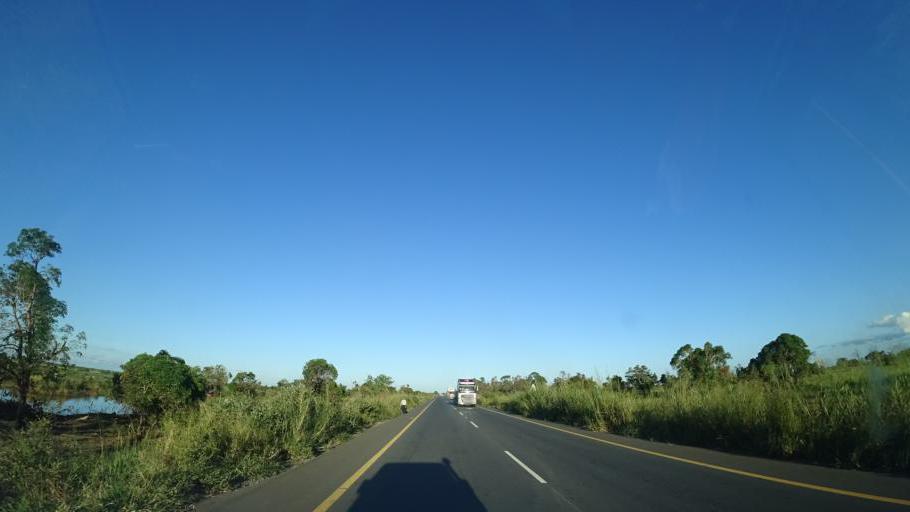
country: MZ
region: Sofala
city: Dondo
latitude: -19.3350
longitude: 34.3255
